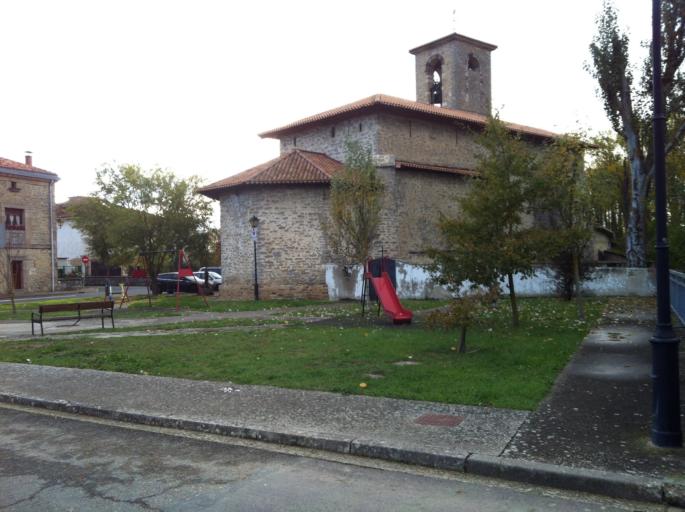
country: ES
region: Basque Country
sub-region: Provincia de Alava
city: Gasteiz / Vitoria
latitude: 42.8644
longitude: -2.7162
